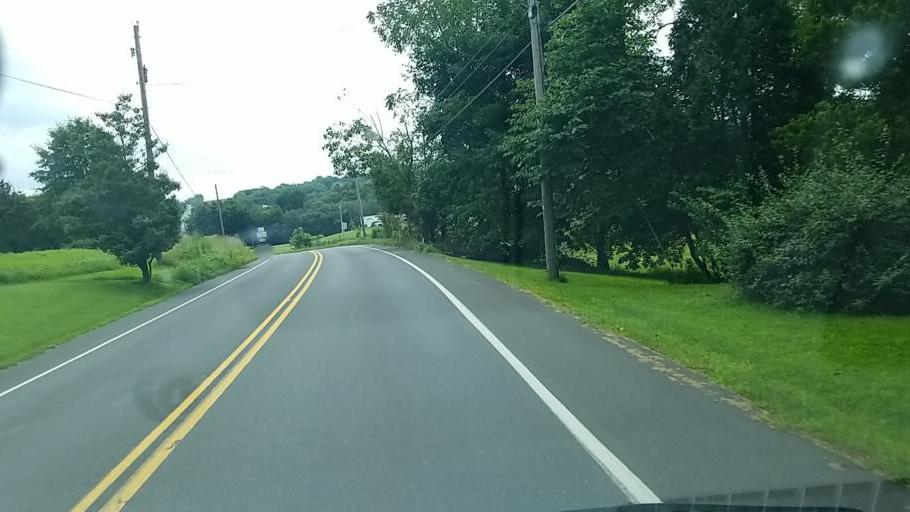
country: US
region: Pennsylvania
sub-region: Dauphin County
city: Elizabethville
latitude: 40.5144
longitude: -76.8672
